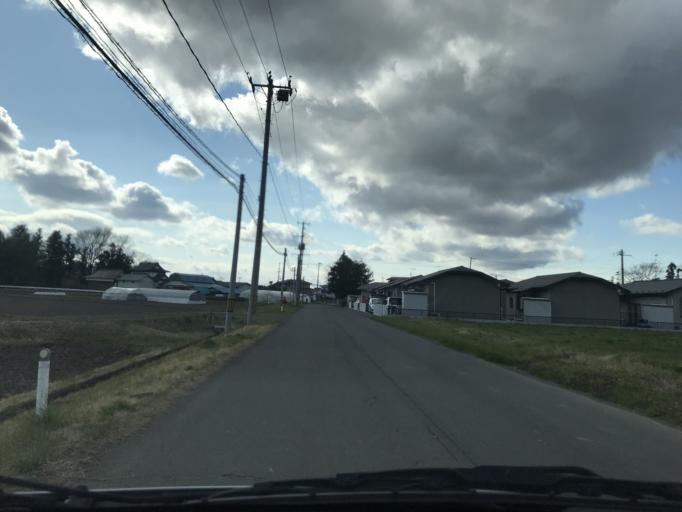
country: JP
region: Miyagi
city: Wakuya
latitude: 38.6652
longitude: 141.1793
